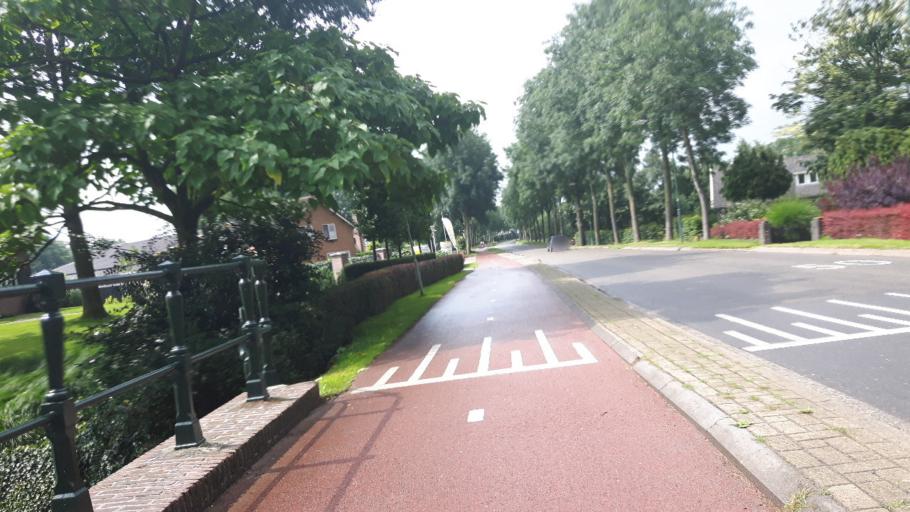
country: NL
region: Utrecht
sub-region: Gemeente Montfoort
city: Montfoort
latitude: 52.0487
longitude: 4.9431
